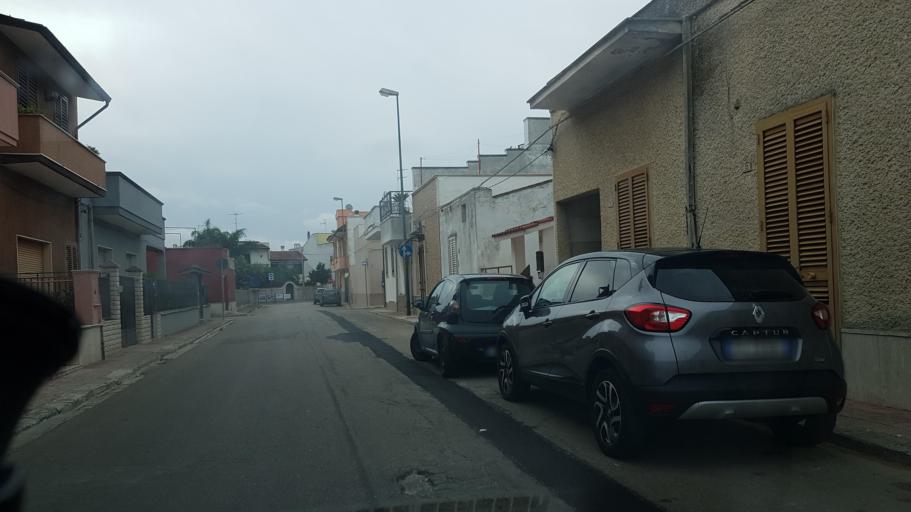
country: IT
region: Apulia
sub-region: Provincia di Brindisi
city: Cellino San Marco
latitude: 40.4699
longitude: 17.9607
